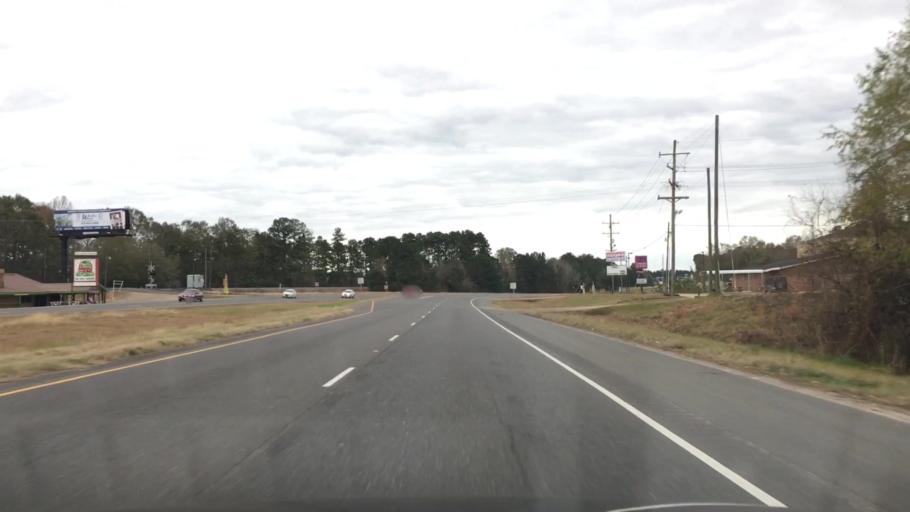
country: US
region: Louisiana
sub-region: Vernon Parish
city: New Llano
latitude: 31.1015
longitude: -93.2696
